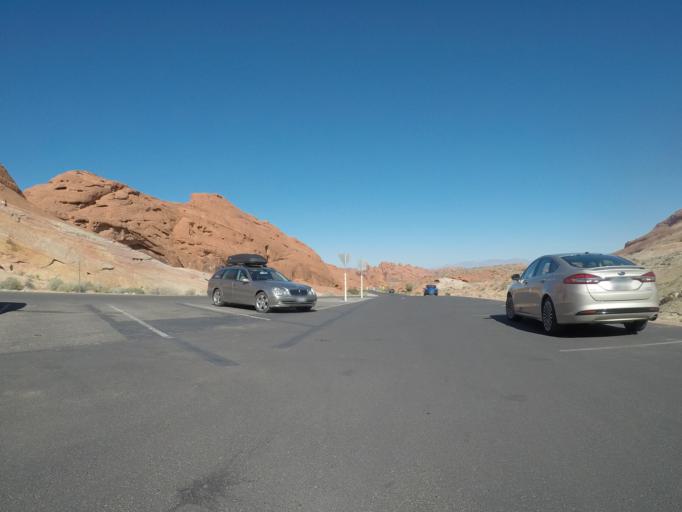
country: US
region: Nevada
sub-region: Clark County
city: Moapa Valley
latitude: 36.4862
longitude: -114.5328
